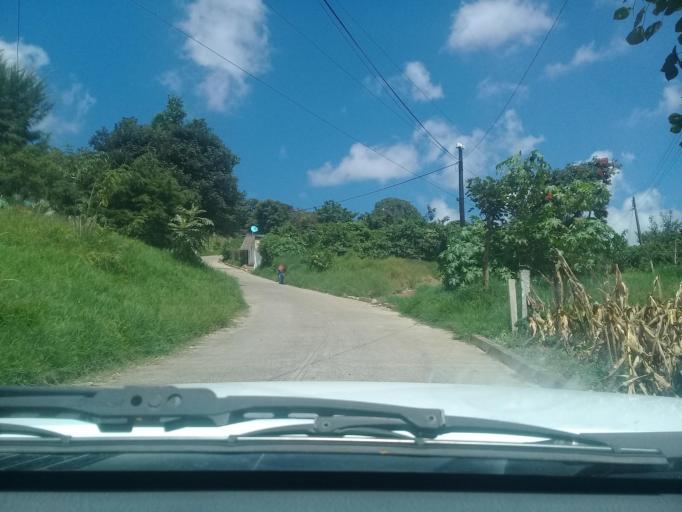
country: MX
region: Veracruz
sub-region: Tlalnelhuayocan
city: Otilpan
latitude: 19.5626
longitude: -96.9788
